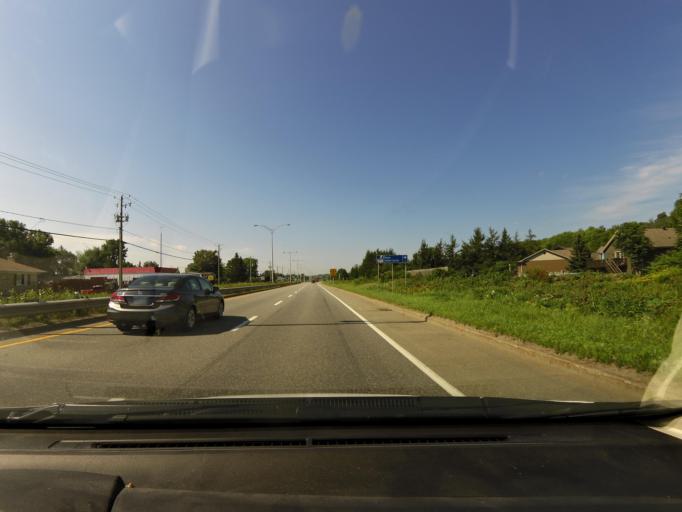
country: CA
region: Quebec
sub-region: Capitale-Nationale
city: Chateau-Richer
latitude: 46.9624
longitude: -71.0293
